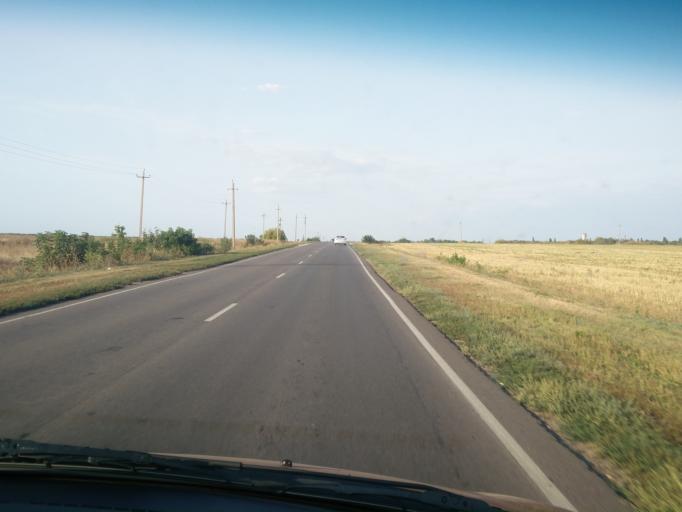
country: RU
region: Voronezj
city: Ramon'
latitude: 51.9305
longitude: 39.3293
